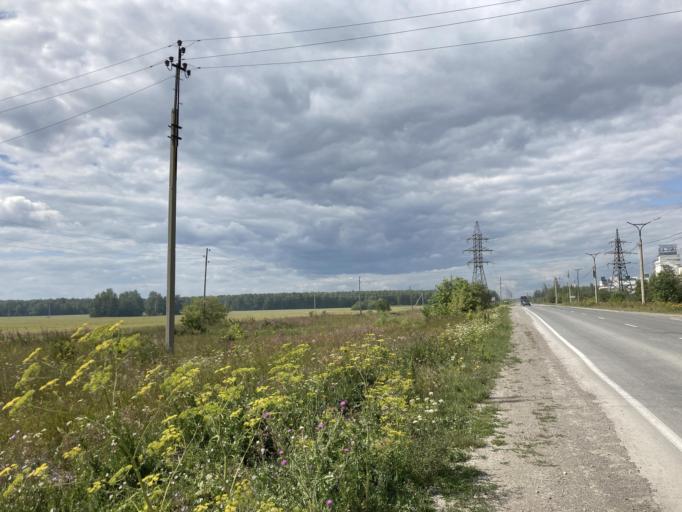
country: RU
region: Sverdlovsk
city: Bogdanovich
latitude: 56.7999
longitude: 62.0386
